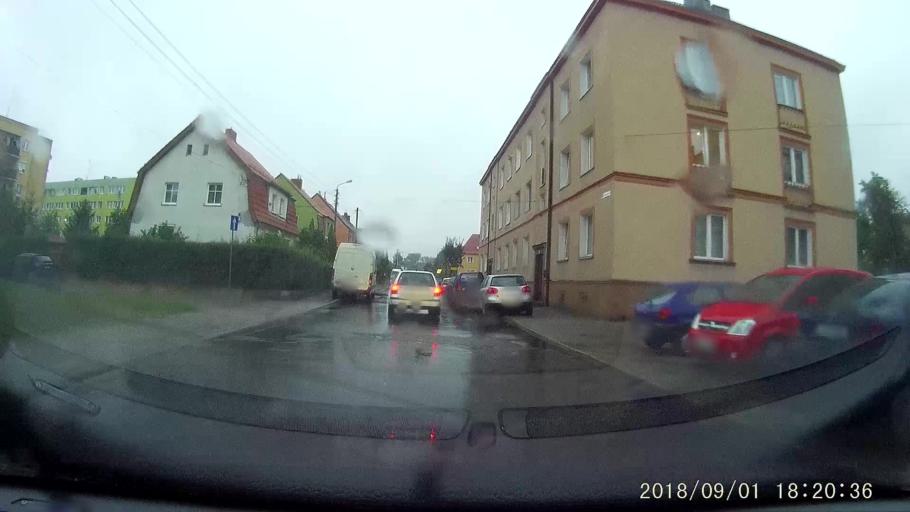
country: PL
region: Lower Silesian Voivodeship
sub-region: Powiat zgorzelecki
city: Piensk
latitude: 51.2502
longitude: 15.0449
